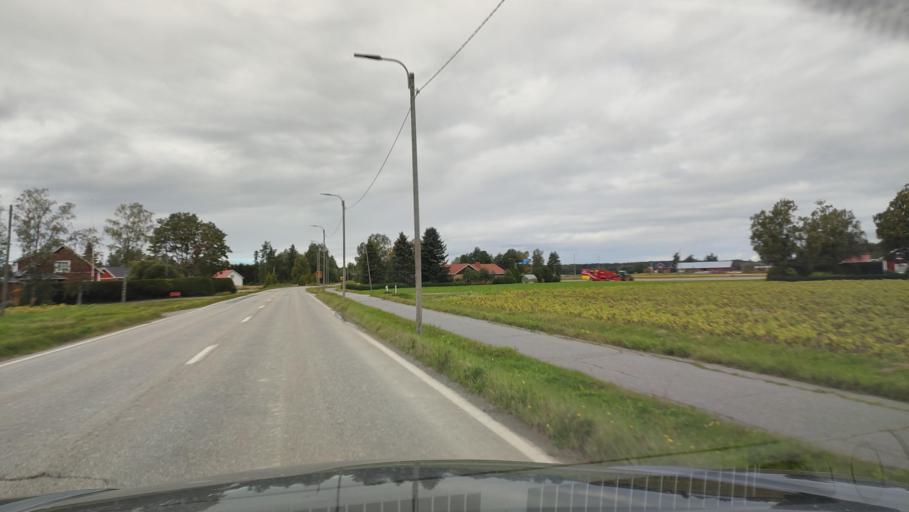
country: FI
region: Ostrobothnia
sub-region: Sydosterbotten
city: Kristinestad
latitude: 62.2580
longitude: 21.4947
